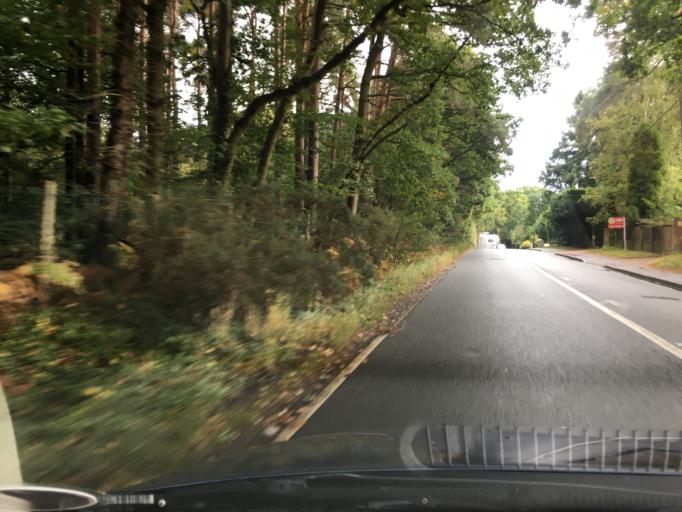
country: GB
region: England
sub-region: Bracknell Forest
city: Crowthorne
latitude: 51.3835
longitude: -0.8034
